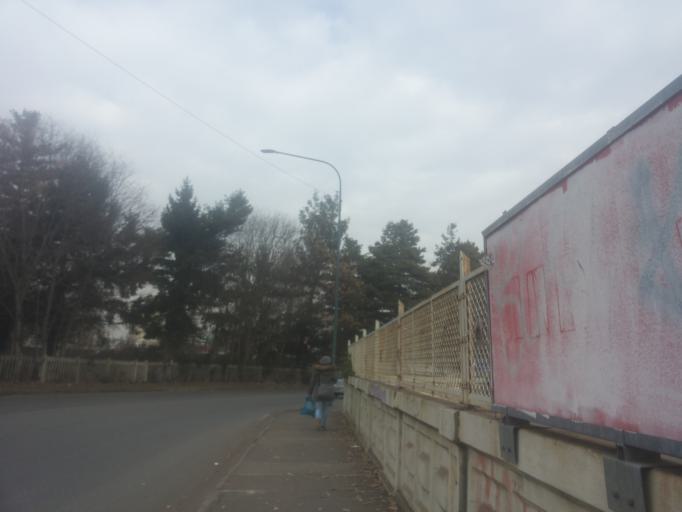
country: IT
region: Piedmont
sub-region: Provincia di Torino
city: Lesna
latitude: 45.0541
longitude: 7.6421
